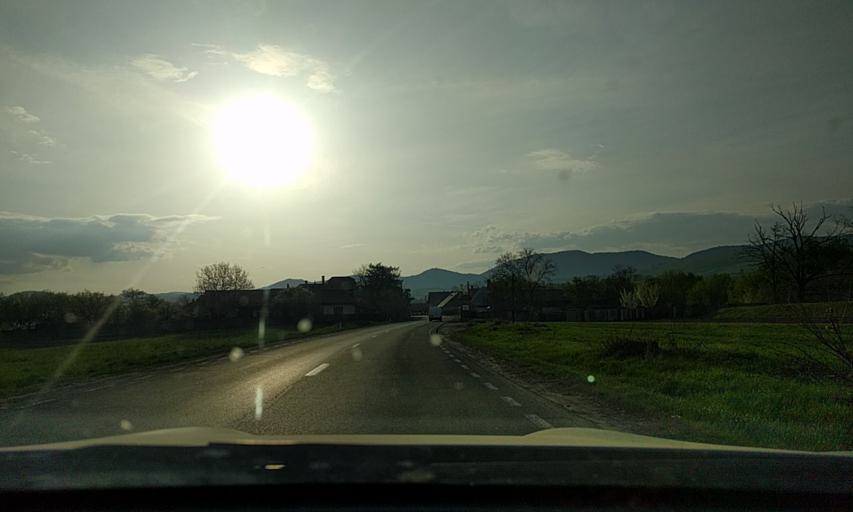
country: RO
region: Covasna
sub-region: Comuna Bretcu
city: Bretcu
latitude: 46.0419
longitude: 26.2880
